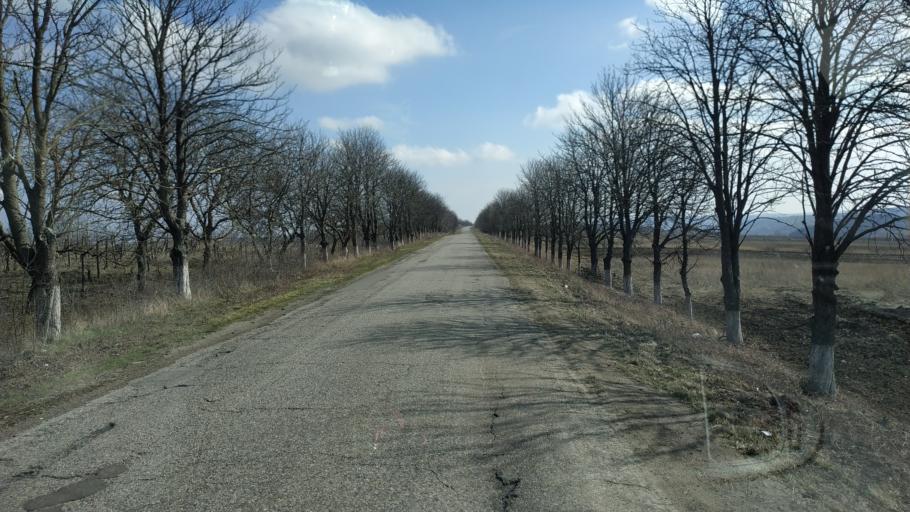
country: MD
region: Hincesti
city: Hincesti
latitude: 46.8546
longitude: 28.6411
